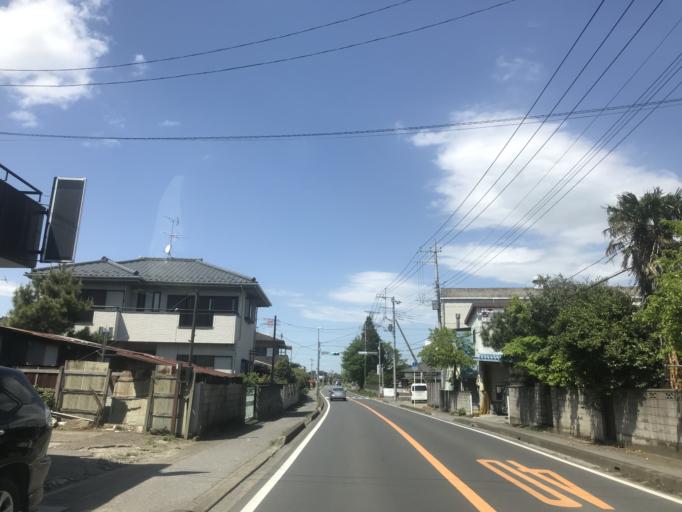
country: JP
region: Chiba
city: Noda
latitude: 35.9500
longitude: 139.9098
